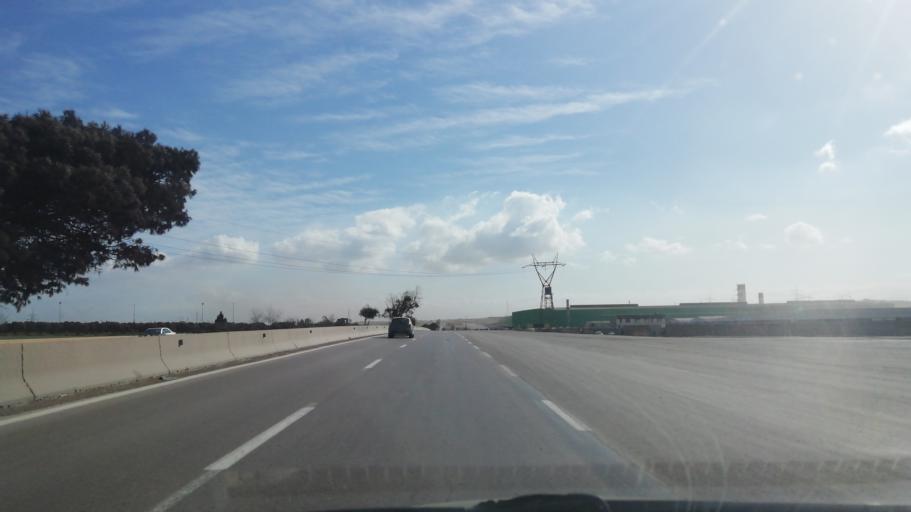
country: DZ
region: Oran
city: Ain el Bya
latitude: 35.7781
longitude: -0.2637
